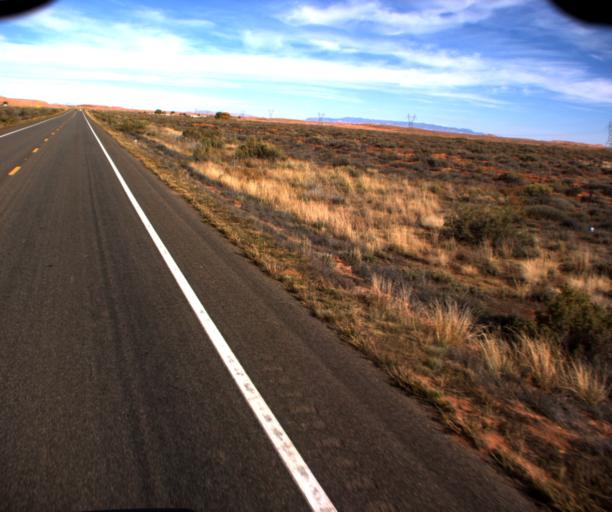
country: US
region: Arizona
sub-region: Navajo County
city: Kayenta
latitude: 36.8116
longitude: -109.8983
